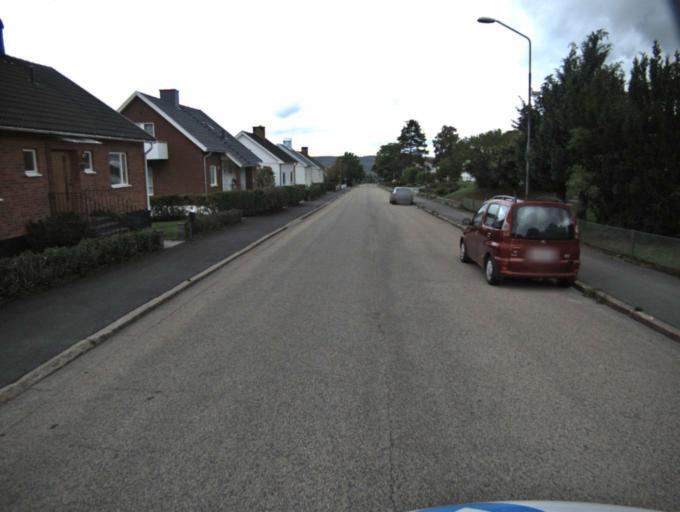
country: SE
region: Vaestra Goetaland
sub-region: Ulricehamns Kommun
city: Ulricehamn
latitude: 57.7818
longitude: 13.4216
